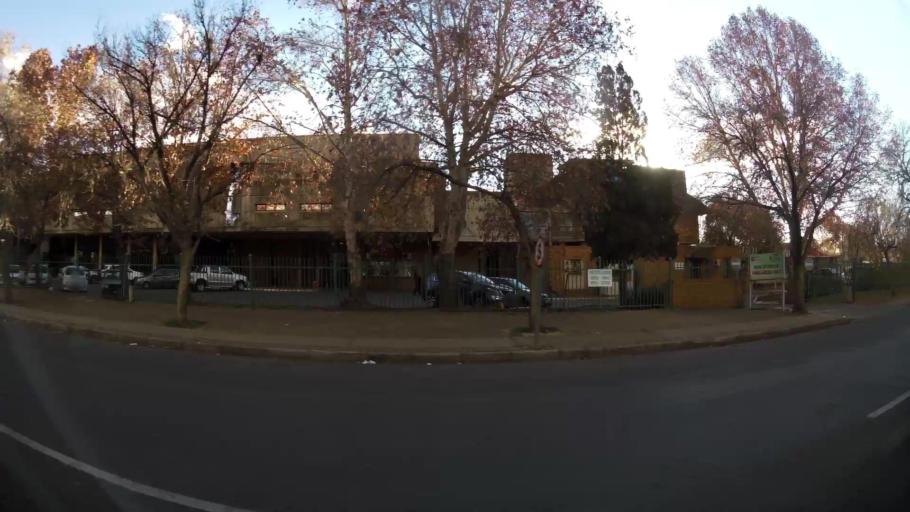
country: ZA
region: North-West
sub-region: Dr Kenneth Kaunda District Municipality
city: Potchefstroom
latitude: -26.7289
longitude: 27.0843
